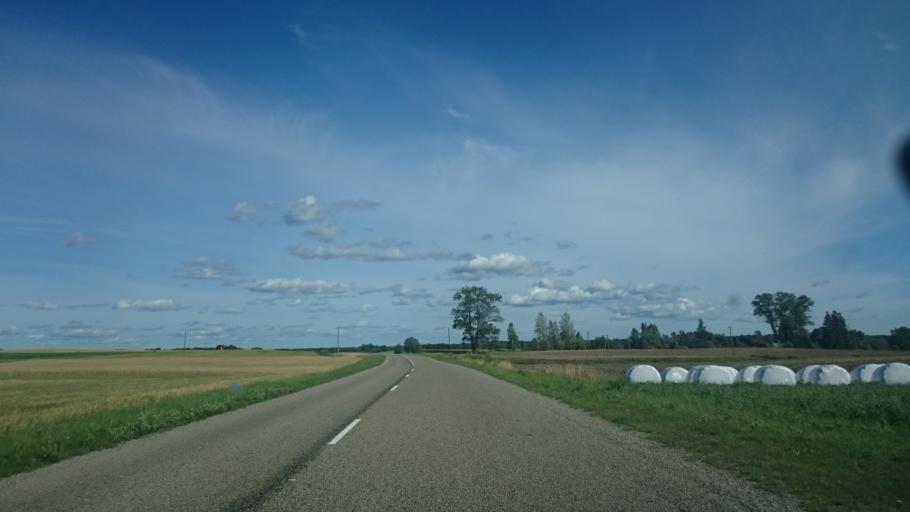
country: LV
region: Aizpute
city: Aizpute
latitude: 56.7011
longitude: 21.7809
